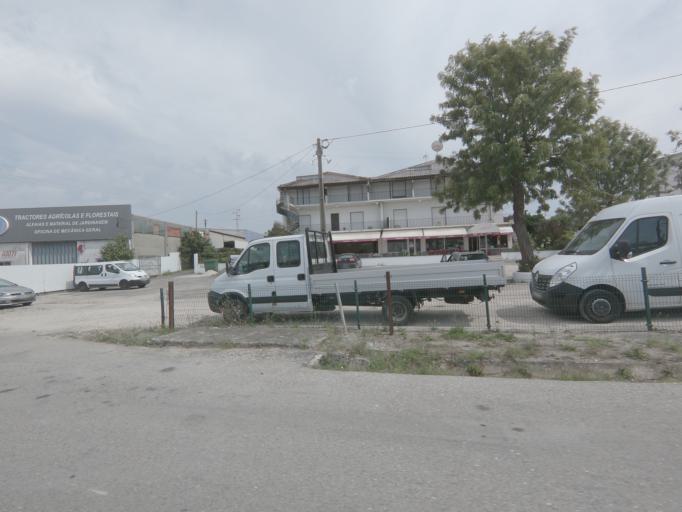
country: PT
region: Leiria
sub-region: Pombal
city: Pombal
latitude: 39.8737
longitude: -8.6881
